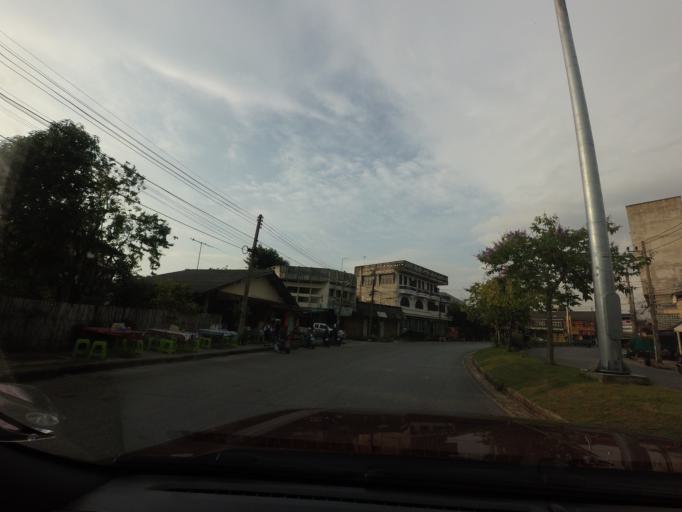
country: TH
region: Pattani
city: Khok Pho
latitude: 6.6784
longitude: 101.1453
